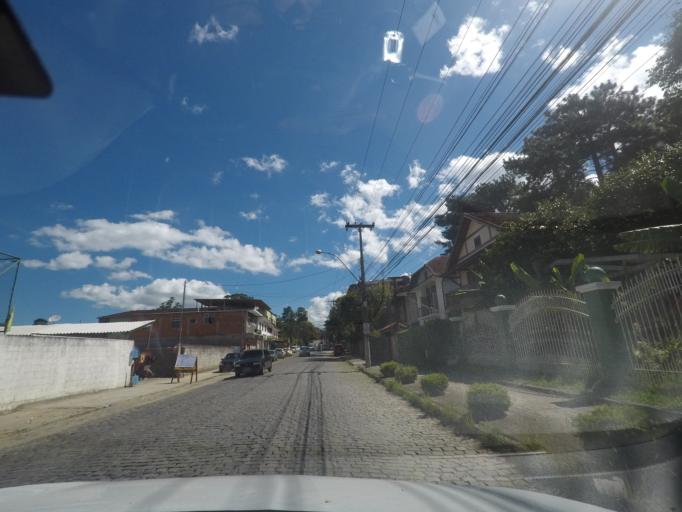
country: BR
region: Rio de Janeiro
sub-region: Teresopolis
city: Teresopolis
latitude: -22.4399
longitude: -42.9776
